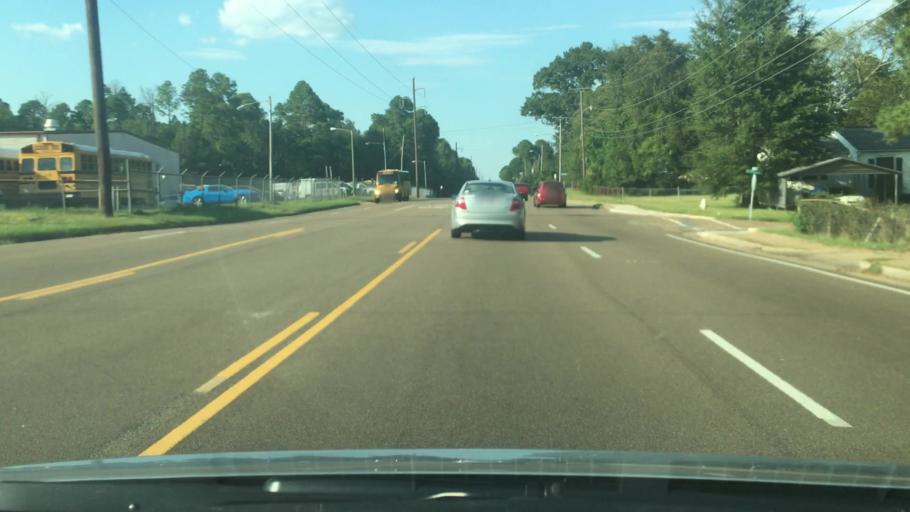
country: US
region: Mississippi
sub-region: Hinds County
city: Jackson
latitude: 32.3588
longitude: -90.1927
